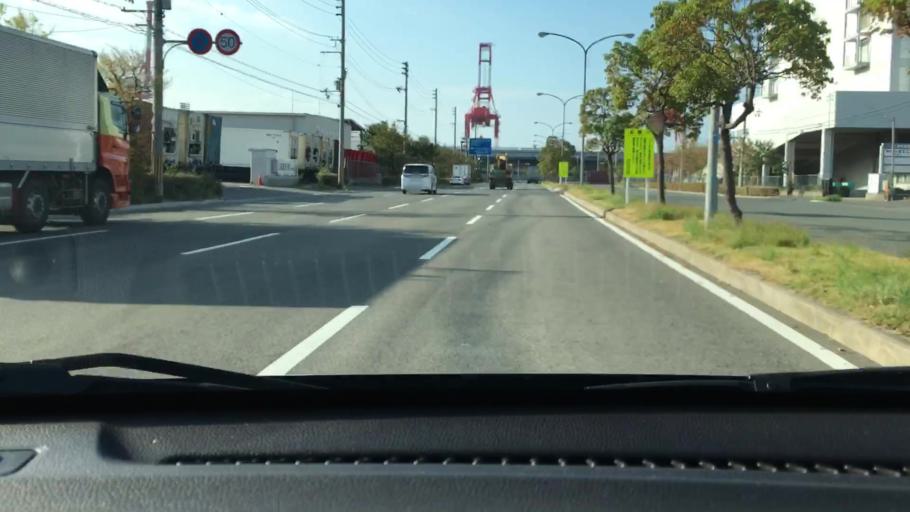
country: JP
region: Hyogo
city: Ashiya
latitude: 34.6863
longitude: 135.2780
